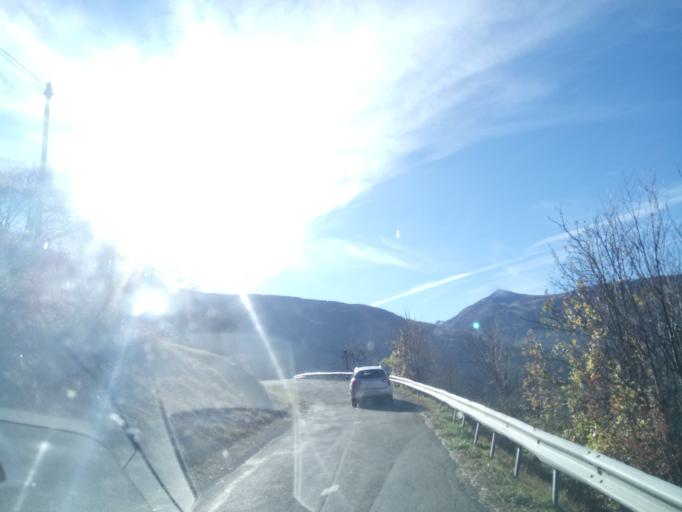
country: FR
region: Rhone-Alpes
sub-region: Departement de la Savoie
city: Saint-Michel-de-Maurienne
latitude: 45.2245
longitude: 6.4830
